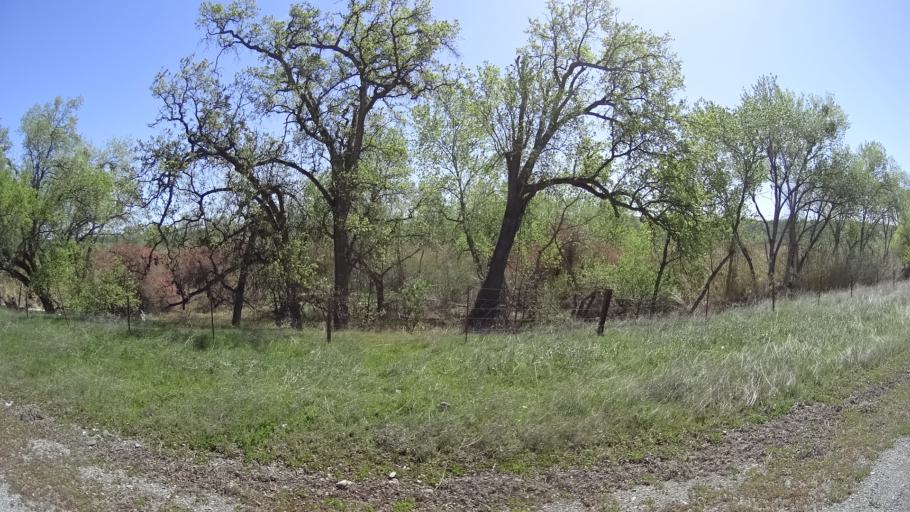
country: US
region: California
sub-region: Glenn County
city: Orland
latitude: 39.7424
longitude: -122.4039
